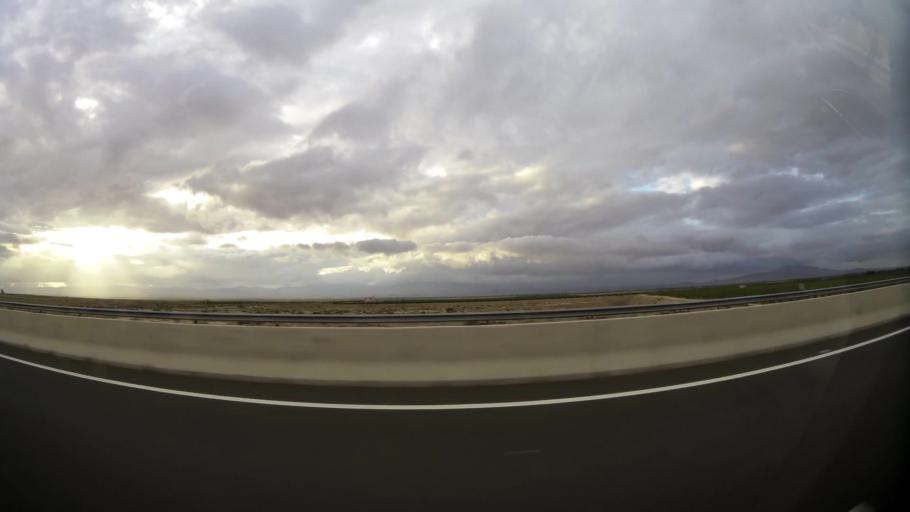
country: MA
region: Taza-Al Hoceima-Taounate
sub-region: Taza
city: Guercif
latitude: 34.3233
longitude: -3.3561
